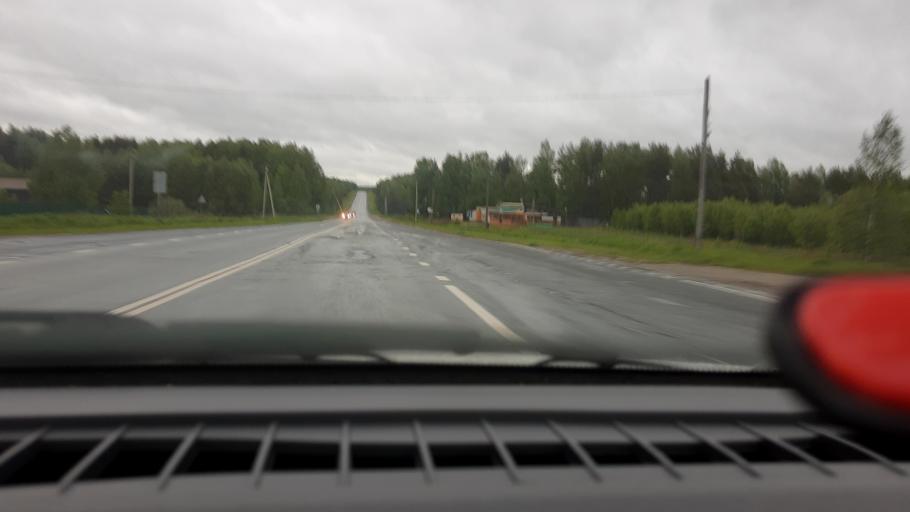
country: RU
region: Nizjnij Novgorod
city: Vladimirskoye
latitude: 56.9721
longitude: 45.1121
